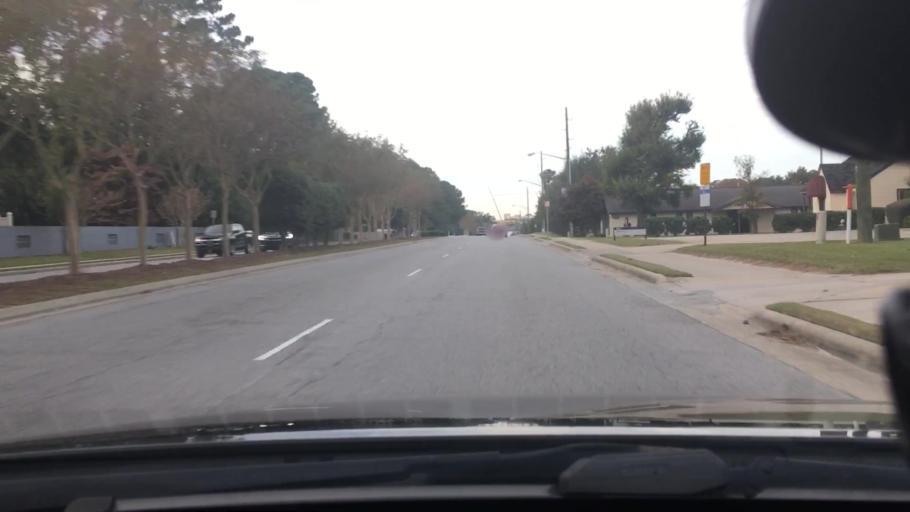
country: US
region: North Carolina
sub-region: Pitt County
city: Greenville
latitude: 35.5942
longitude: -77.3692
